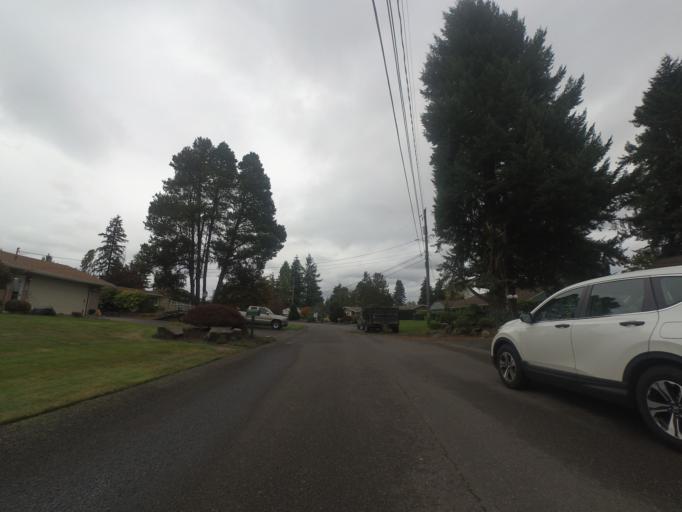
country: US
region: Washington
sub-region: Pierce County
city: Lakewood
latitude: 47.1541
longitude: -122.5190
